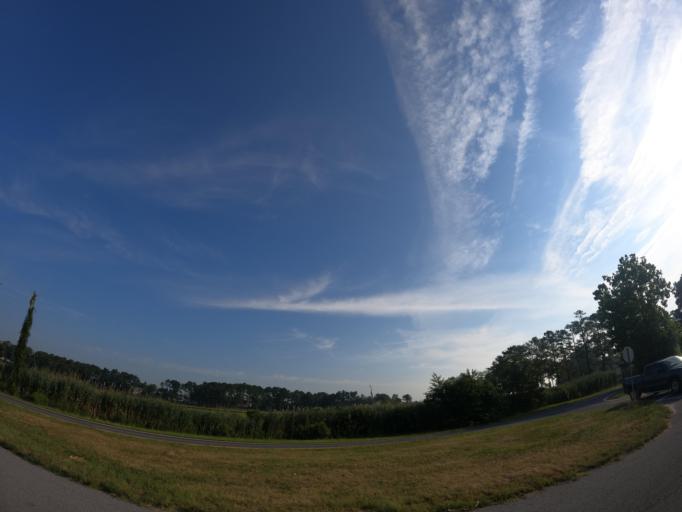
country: US
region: Delaware
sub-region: Sussex County
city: Long Neck
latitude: 38.5570
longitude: -75.2003
